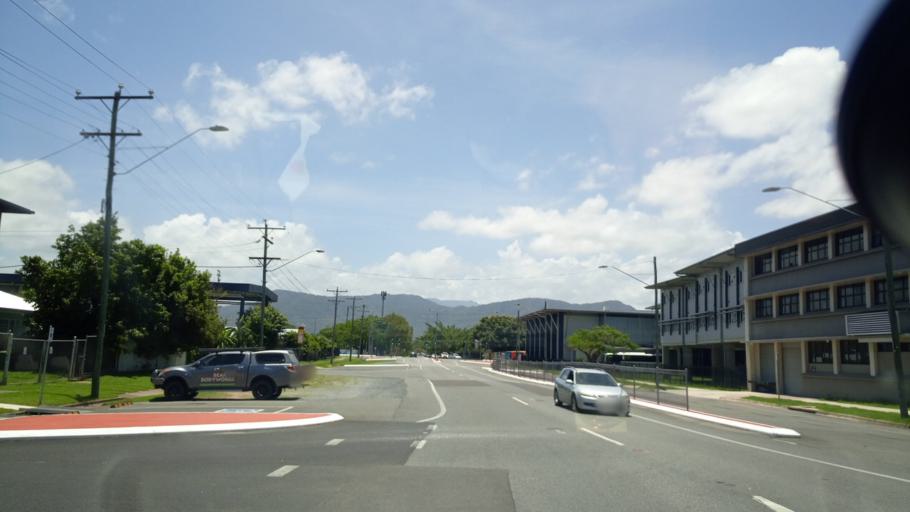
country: AU
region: Queensland
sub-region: Cairns
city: Cairns
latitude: -16.9274
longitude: 145.7687
